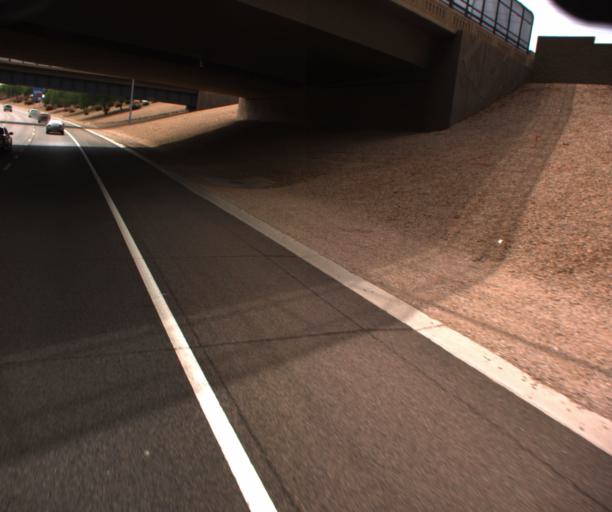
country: US
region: Arizona
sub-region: Maricopa County
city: Gilbert
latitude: 33.3219
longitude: -111.7381
